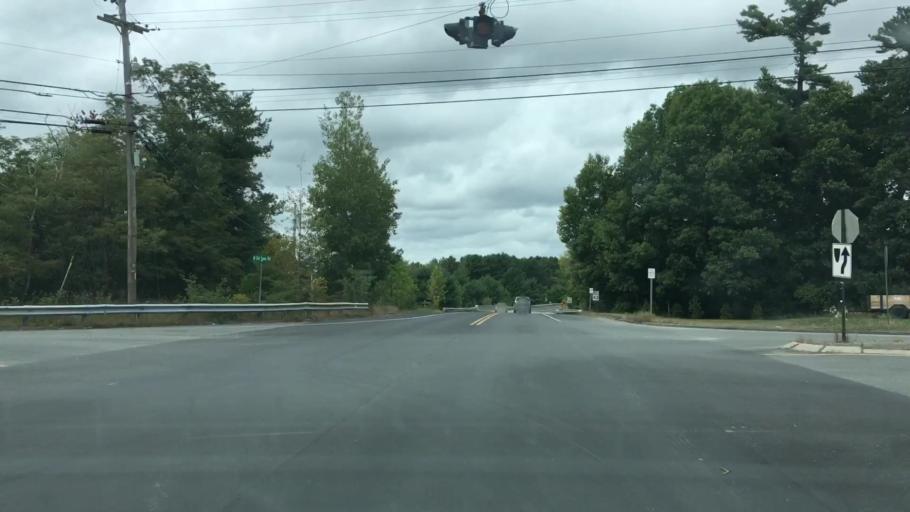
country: US
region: Maine
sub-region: Penobscot County
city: Milford
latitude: 44.9525
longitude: -68.6990
